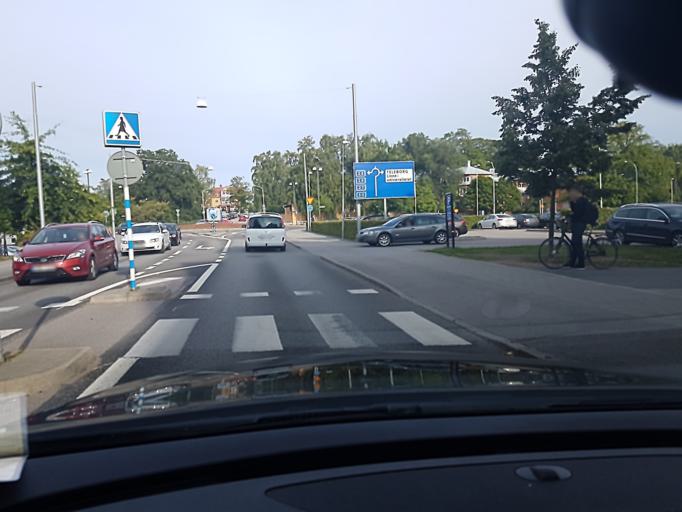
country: SE
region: Kronoberg
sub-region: Vaxjo Kommun
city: Vaexjoe
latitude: 56.8782
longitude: 14.8133
